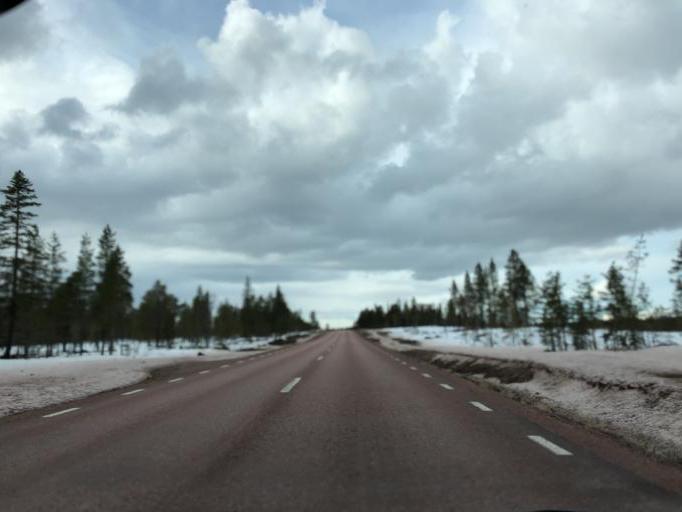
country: SE
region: Dalarna
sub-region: Alvdalens Kommun
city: AElvdalen
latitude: 61.4049
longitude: 13.4900
